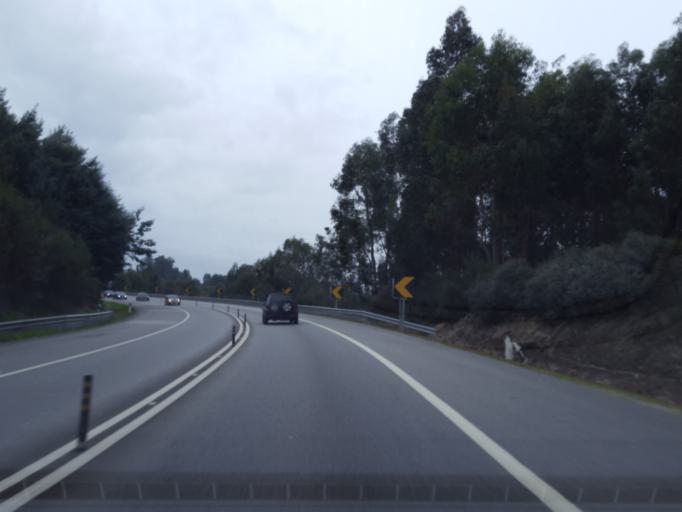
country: PT
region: Porto
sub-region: Marco de Canaveses
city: Marco de Canavezes
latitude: 41.2205
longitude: -8.1859
